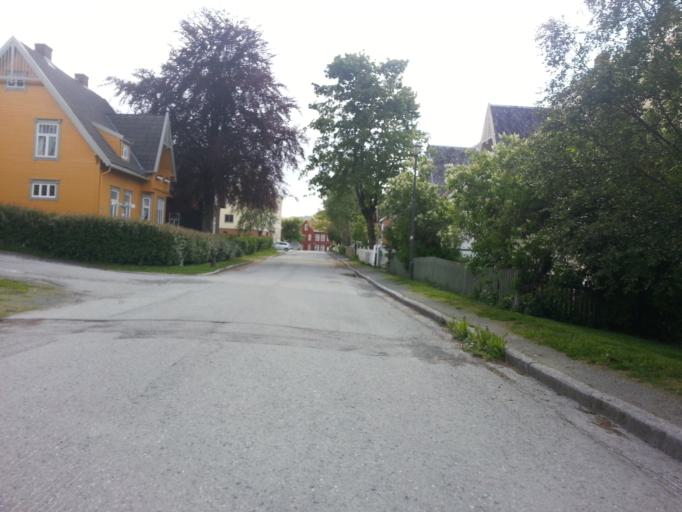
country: NO
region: Sor-Trondelag
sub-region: Trondheim
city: Trondheim
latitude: 63.4227
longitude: 10.4057
